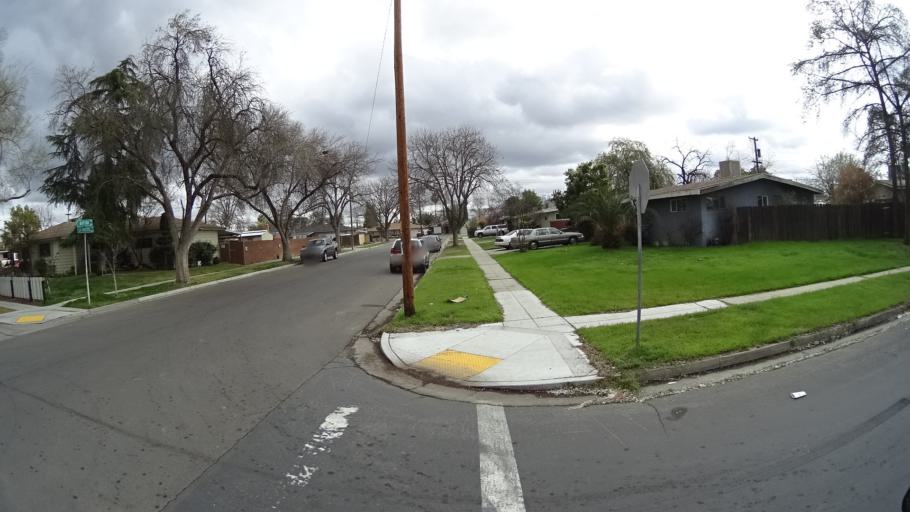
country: US
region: California
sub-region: Fresno County
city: Fresno
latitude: 36.7828
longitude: -119.8367
